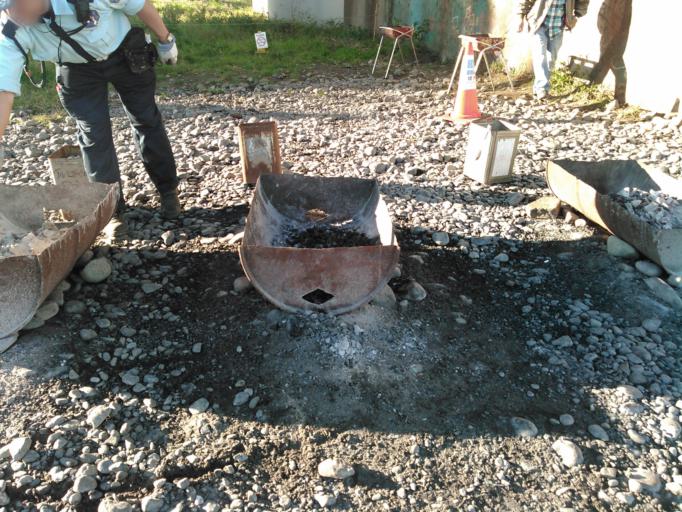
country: JP
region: Tokyo
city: Chofugaoka
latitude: 35.6089
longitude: 139.6244
